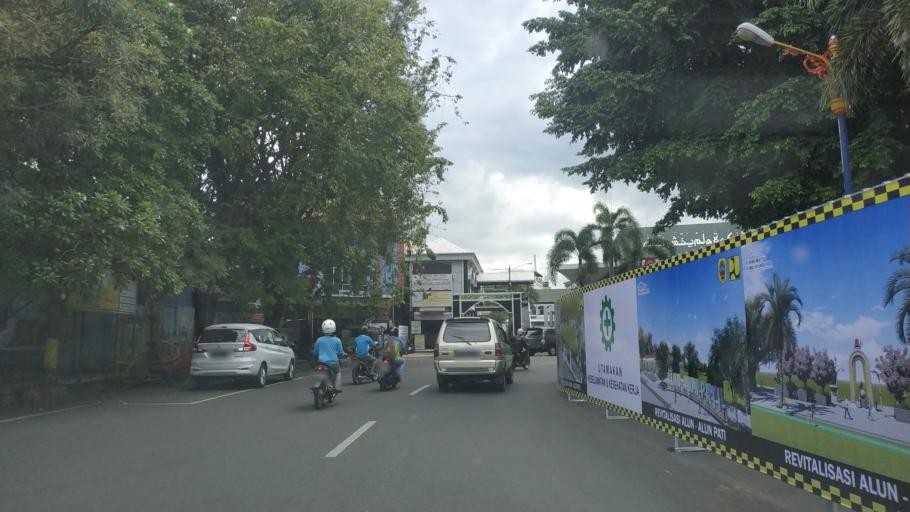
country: ID
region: Central Java
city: Pati
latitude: -6.7541
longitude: 111.0398
